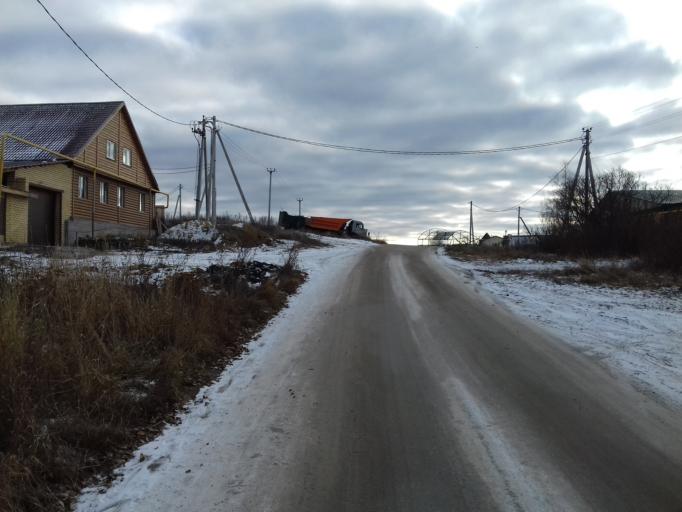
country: RU
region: Sverdlovsk
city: Istok
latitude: 56.7439
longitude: 60.7006
